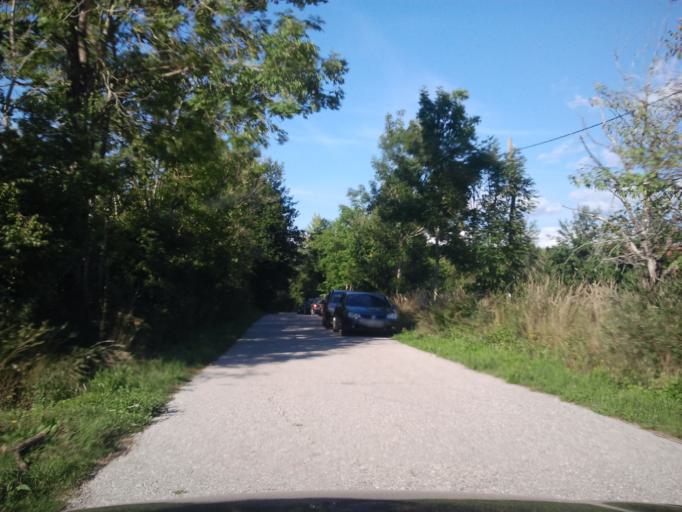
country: HR
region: Zadarska
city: Obrovac
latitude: 44.3341
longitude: 15.6416
